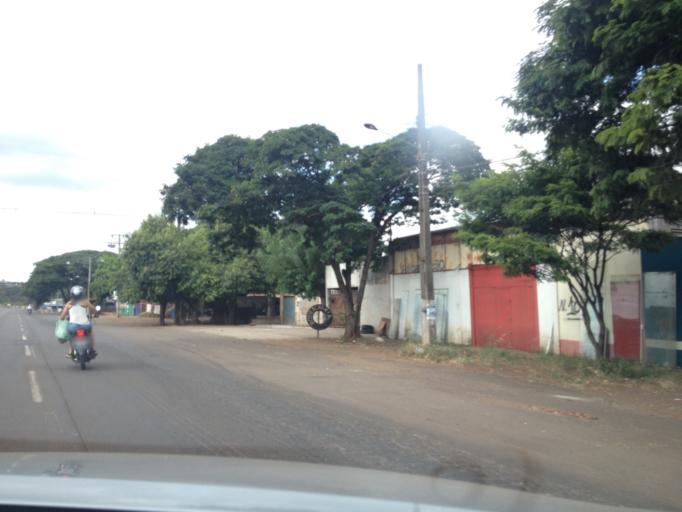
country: BR
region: Parana
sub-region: Sarandi
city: Sarandi
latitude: -23.4417
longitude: -51.8952
